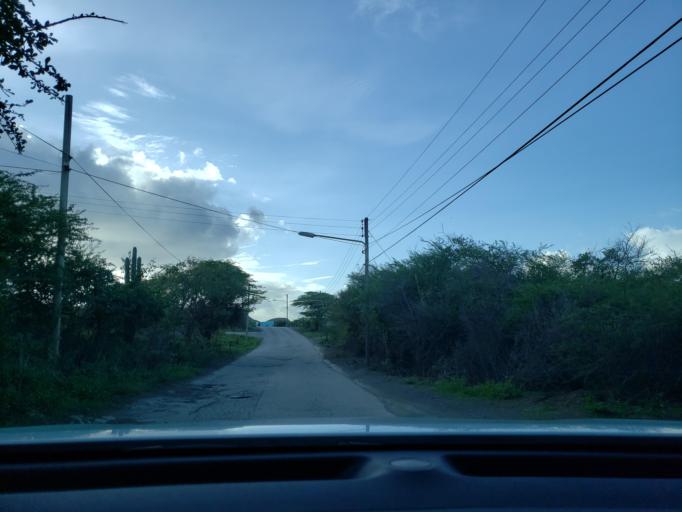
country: CW
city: Dorp Soto
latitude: 12.2172
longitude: -69.0693
